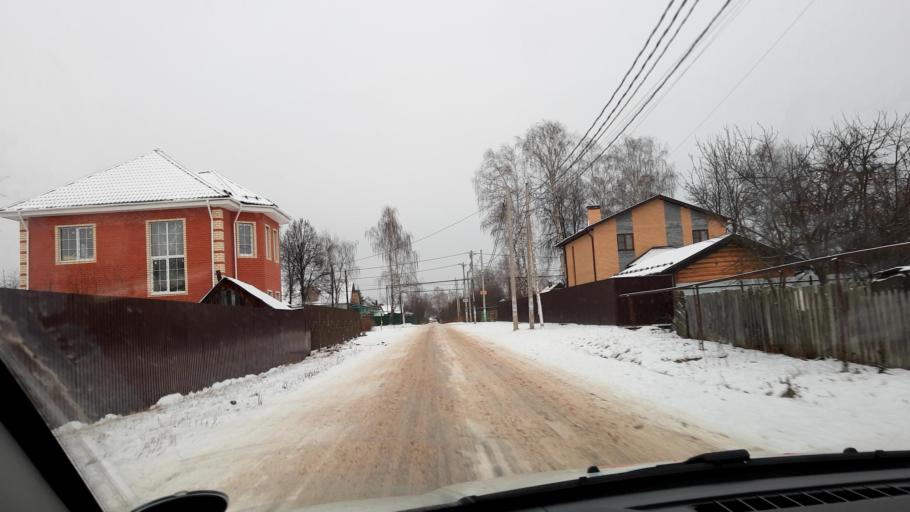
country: RU
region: Nizjnij Novgorod
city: Burevestnik
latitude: 56.1997
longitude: 43.7715
